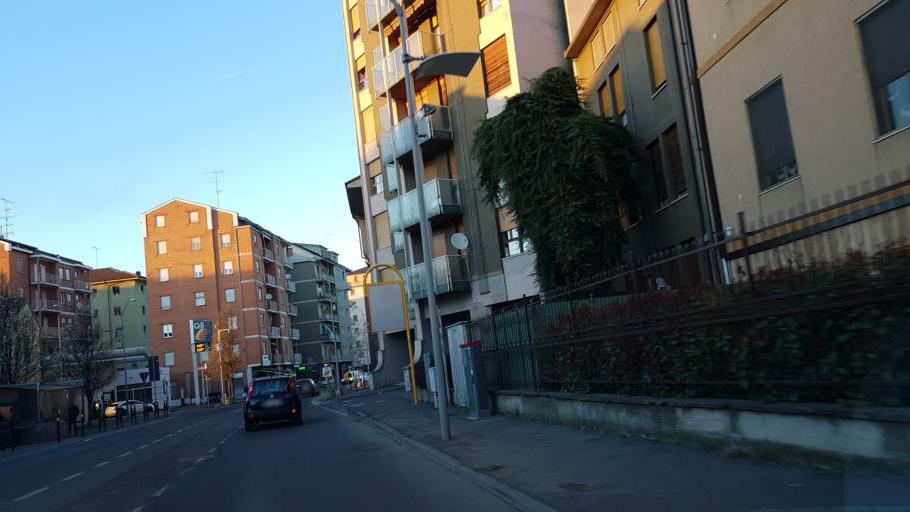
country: IT
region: Piedmont
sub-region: Provincia di Alessandria
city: Tortona
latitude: 44.8888
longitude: 8.8595
